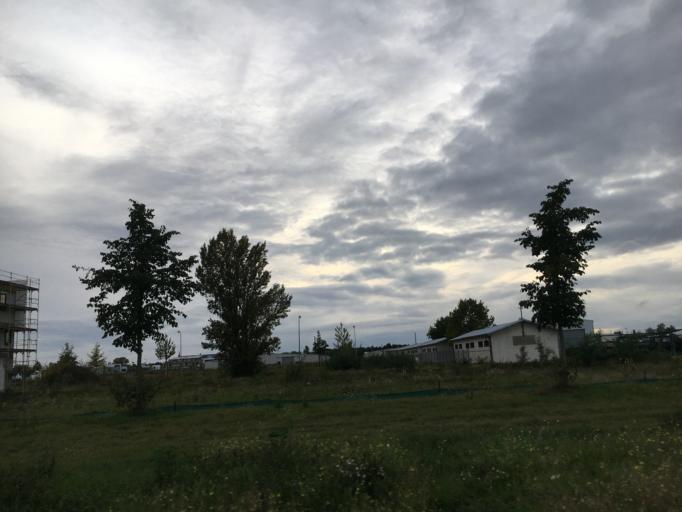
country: DE
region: Baden-Wuerttemberg
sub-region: Karlsruhe Region
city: Eggenstein-Leopoldshafen
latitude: 49.0583
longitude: 8.4000
